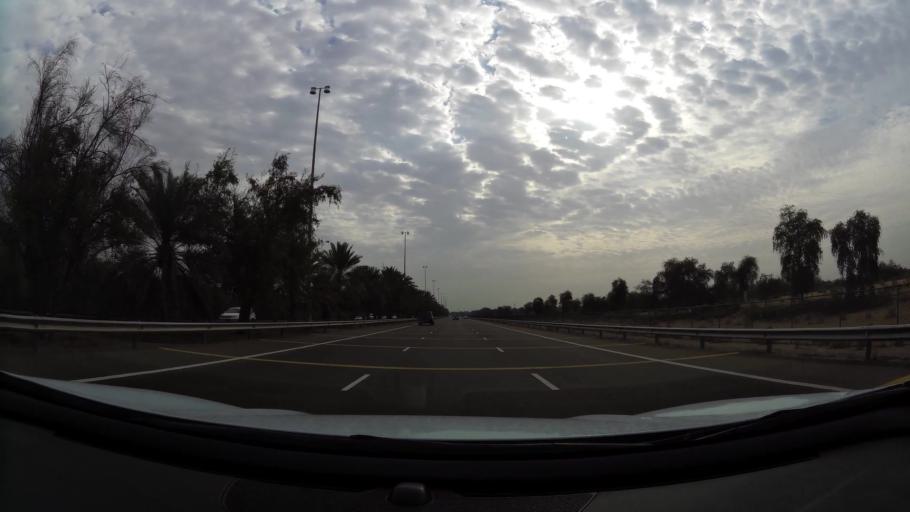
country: AE
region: Abu Dhabi
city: Al Ain
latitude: 24.1790
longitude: 55.1705
